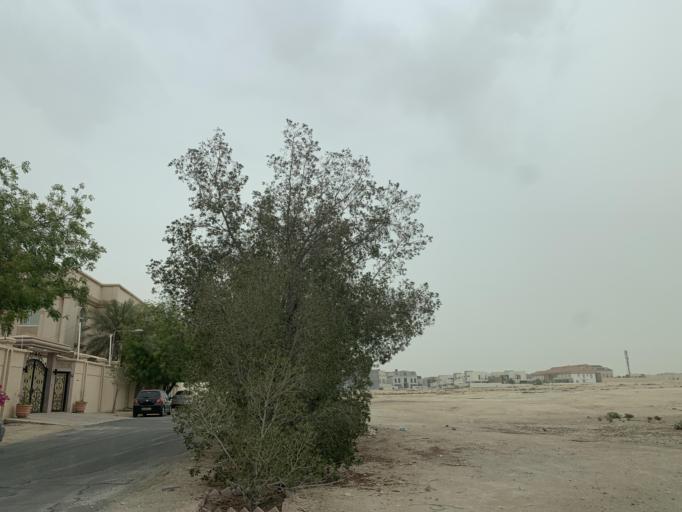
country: BH
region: Central Governorate
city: Madinat Hamad
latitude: 26.1456
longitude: 50.5234
